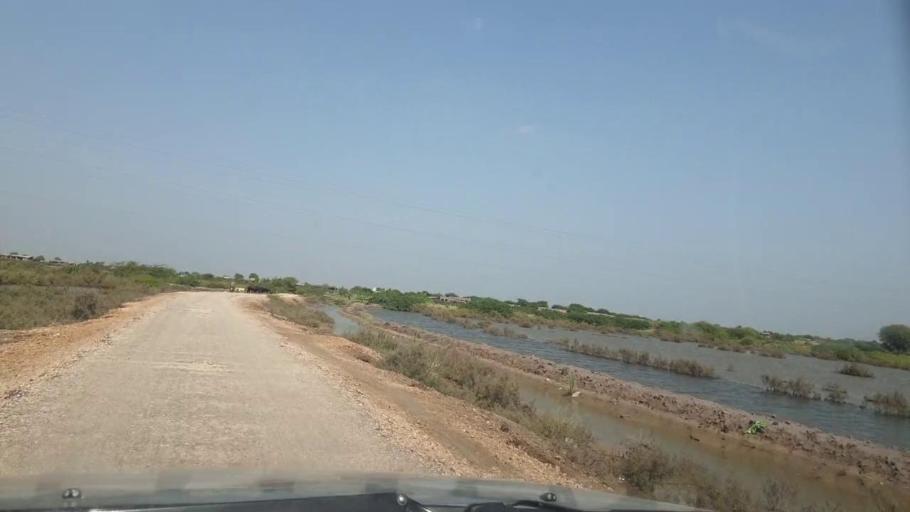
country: PK
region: Sindh
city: Tando Ghulam Ali
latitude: 25.0692
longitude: 68.8011
